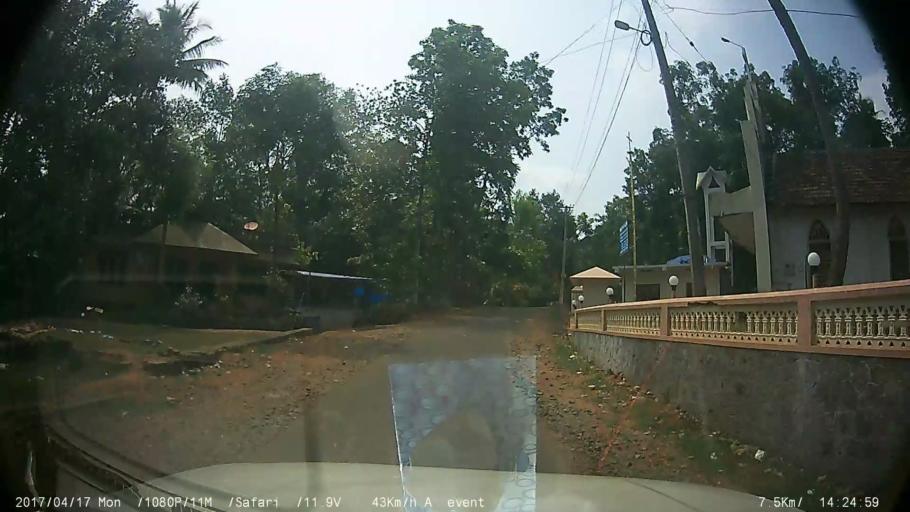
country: IN
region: Kerala
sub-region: Kottayam
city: Palackattumala
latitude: 9.7900
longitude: 76.5606
